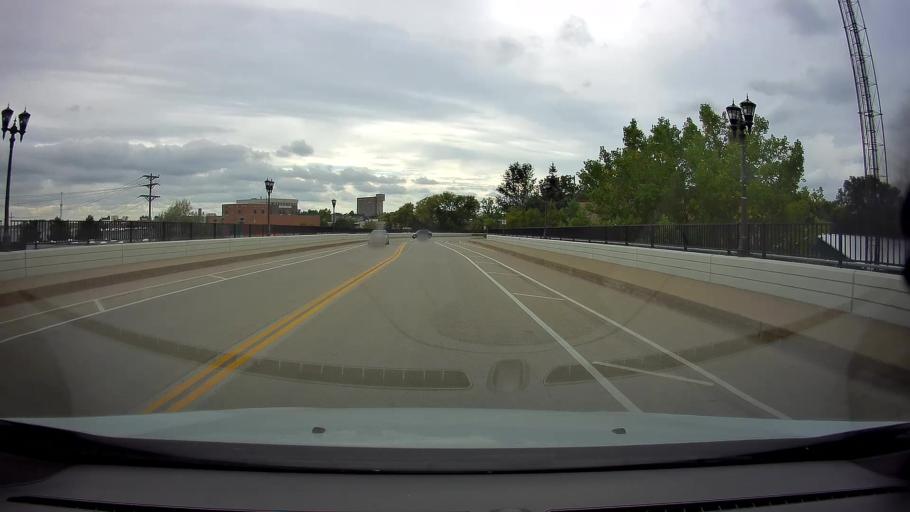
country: US
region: Minnesota
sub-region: Ramsey County
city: Lauderdale
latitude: 44.9728
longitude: -93.1958
